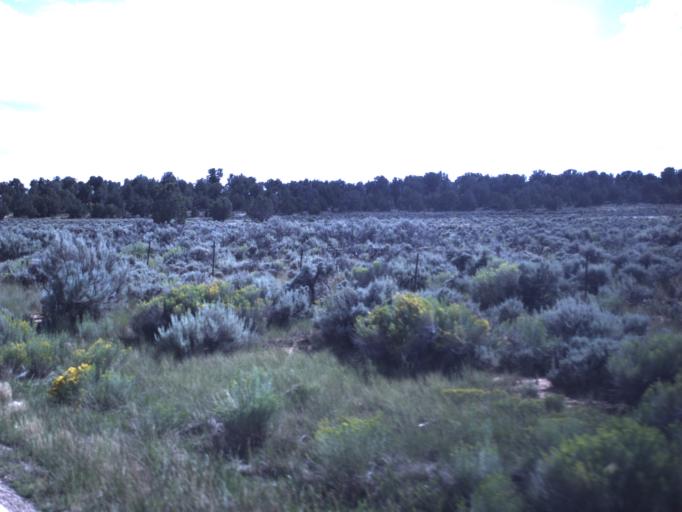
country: US
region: Utah
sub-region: Duchesne County
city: Duchesne
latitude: 40.2975
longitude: -110.6958
